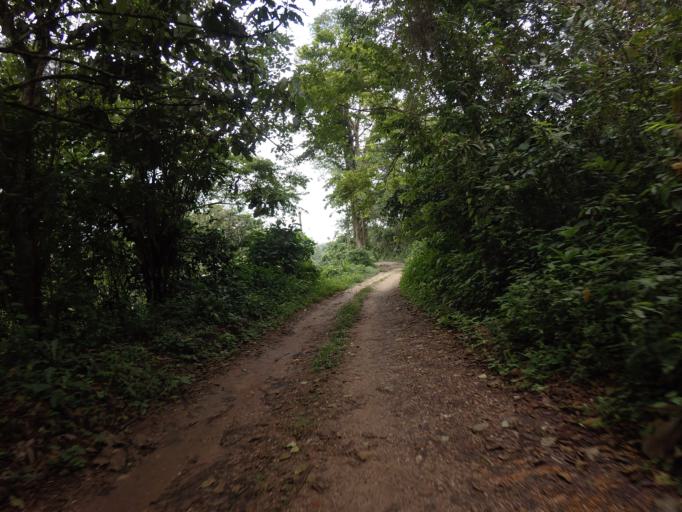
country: TG
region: Plateaux
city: Kpalime
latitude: 6.8439
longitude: 0.4431
